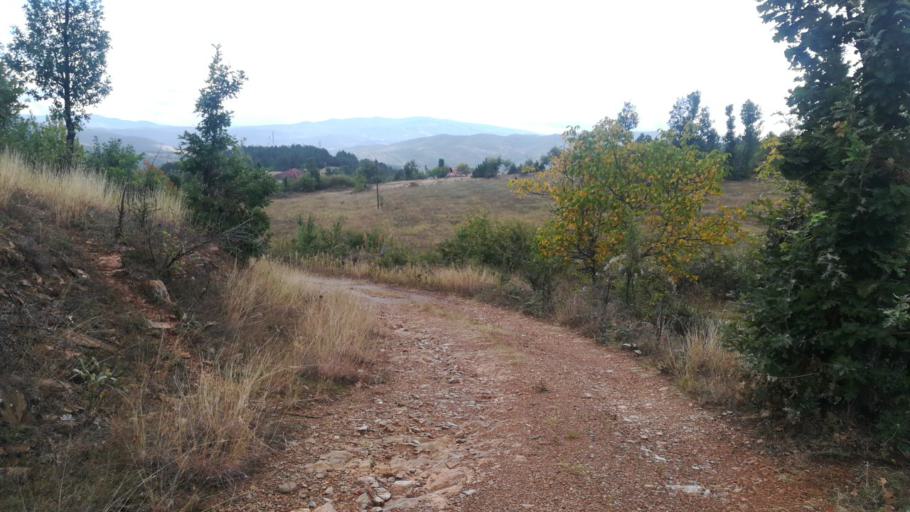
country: MK
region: Makedonska Kamenica
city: Makedonska Kamenica
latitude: 42.0163
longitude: 22.5751
